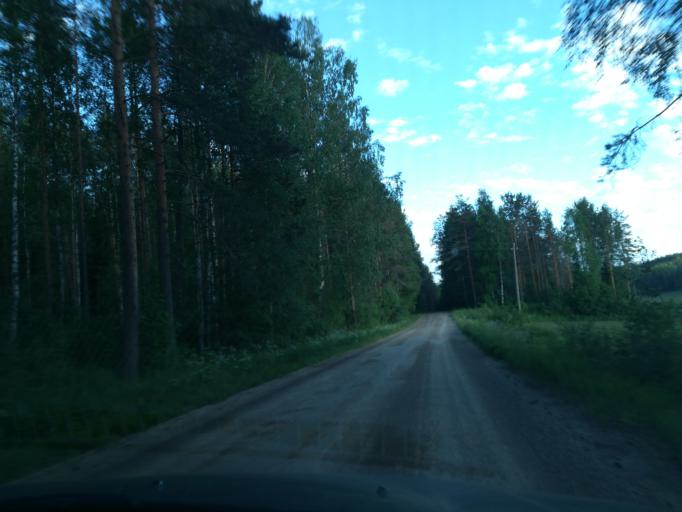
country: FI
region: Southern Savonia
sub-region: Mikkeli
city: Puumala
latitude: 61.6061
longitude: 28.1166
